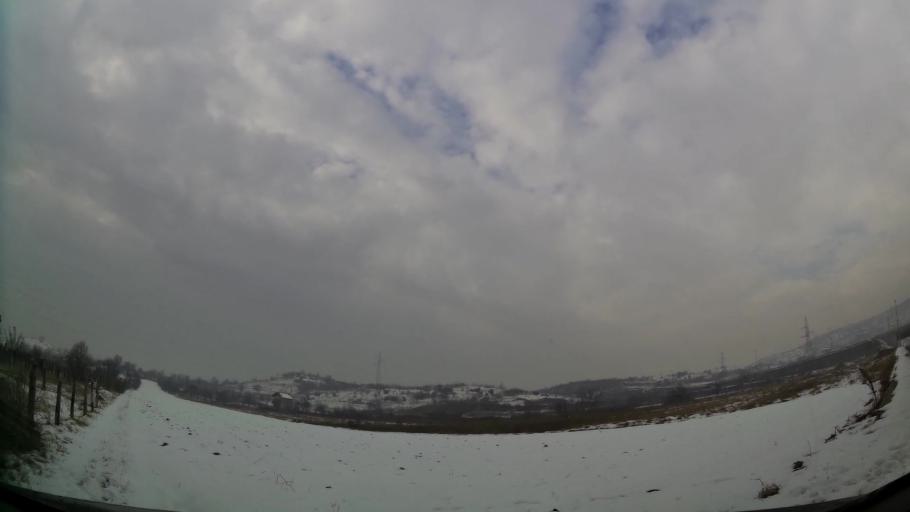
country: MK
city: Kondovo
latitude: 42.0373
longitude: 21.3380
